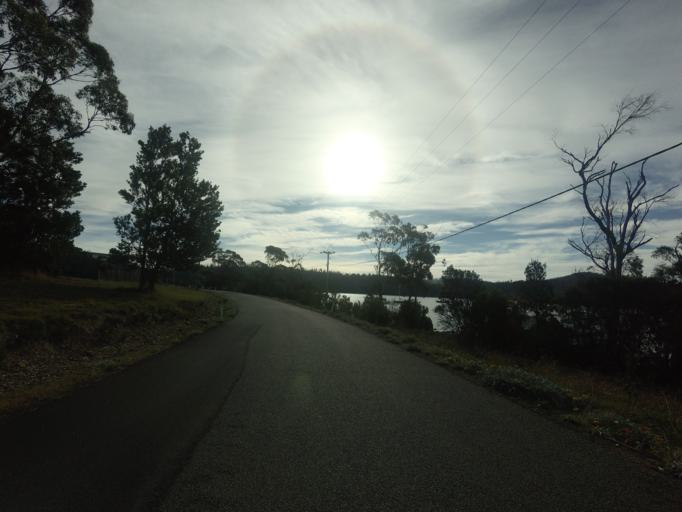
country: AU
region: Tasmania
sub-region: Sorell
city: Sorell
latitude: -42.9462
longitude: 147.8602
